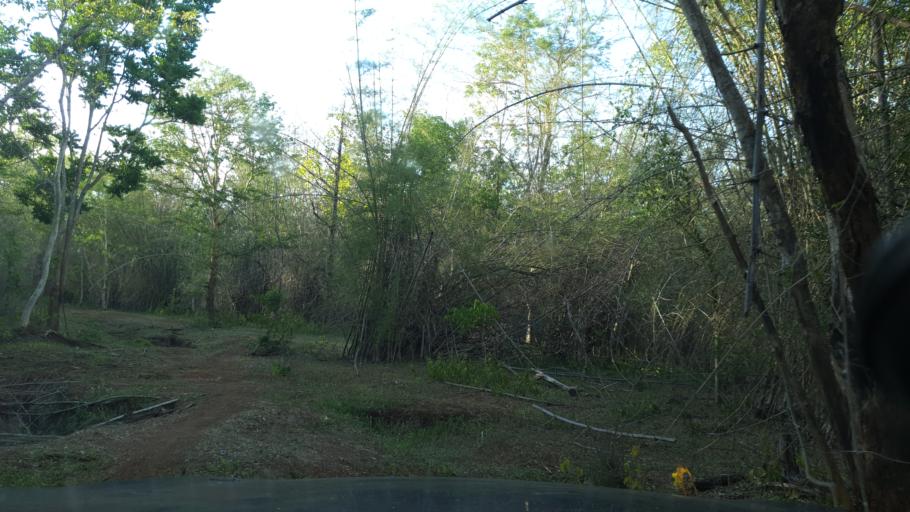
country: TH
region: Lampang
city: Sop Prap
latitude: 17.9662
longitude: 99.3512
